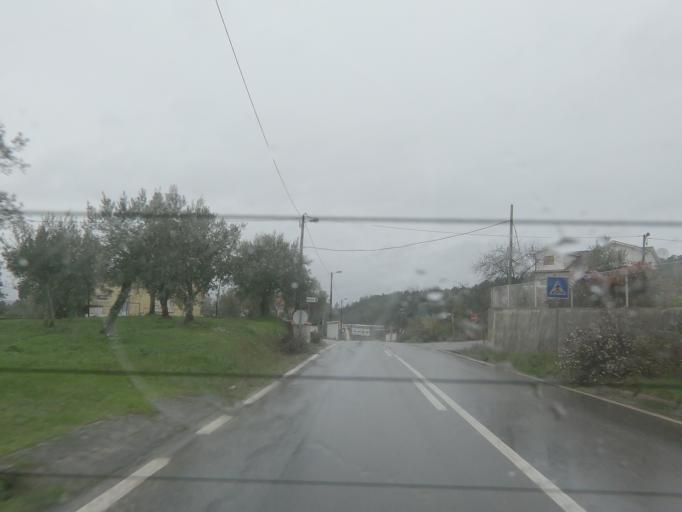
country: PT
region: Vila Real
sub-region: Sabrosa
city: Vilela
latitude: 41.2361
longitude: -7.6824
